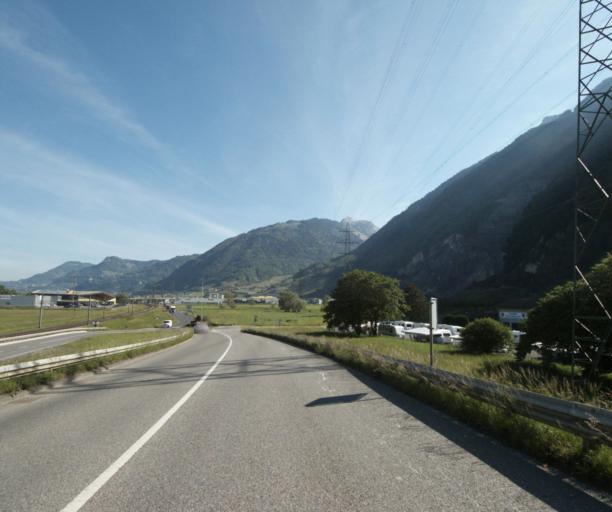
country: CH
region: Vaud
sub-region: Aigle District
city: Villeneuve
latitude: 46.3785
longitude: 6.9284
